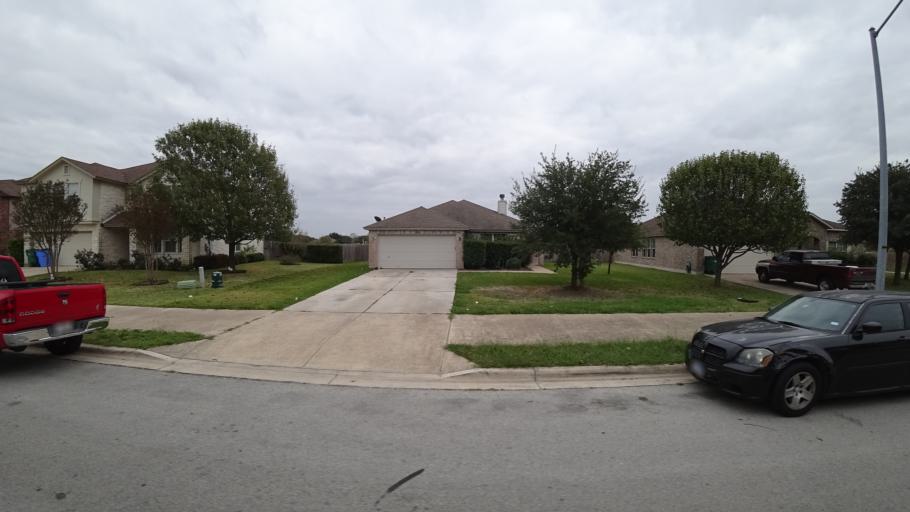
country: US
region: Texas
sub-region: Travis County
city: Pflugerville
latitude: 30.4559
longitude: -97.6215
